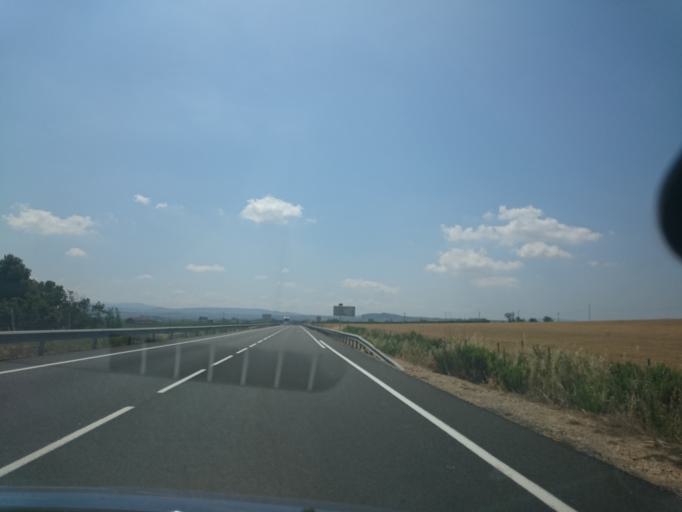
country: ES
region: Catalonia
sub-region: Provincia de Barcelona
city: Sant Pere de Riudebitlles
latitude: 41.4264
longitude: 1.6829
